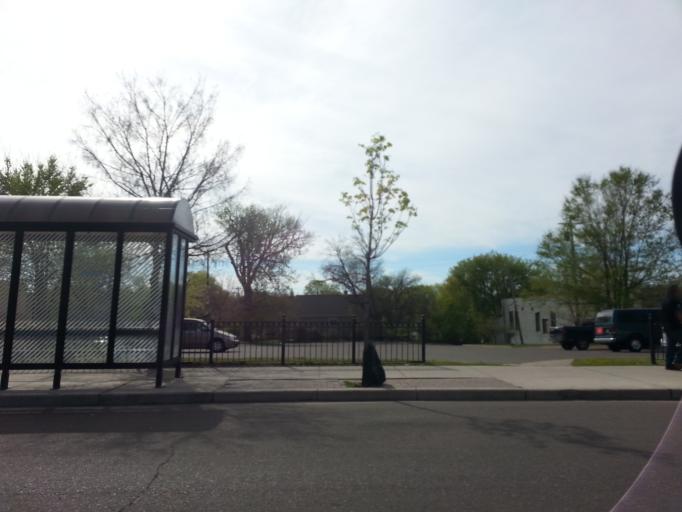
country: US
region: Minnesota
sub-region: Ramsey County
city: Saint Paul
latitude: 44.9686
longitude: -93.0736
